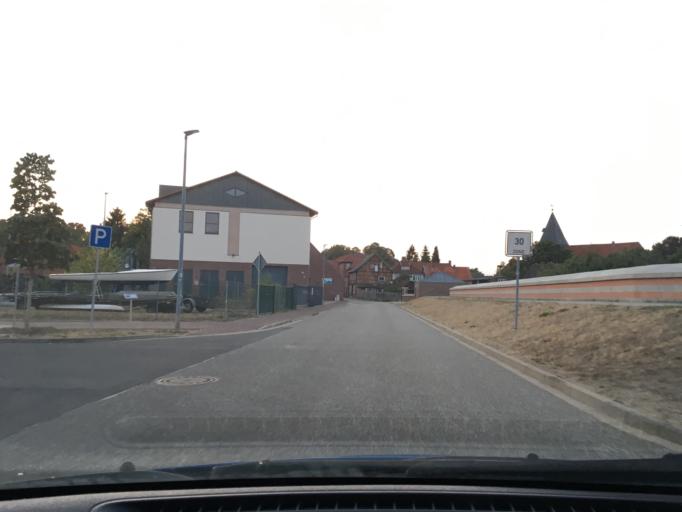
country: DE
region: Lower Saxony
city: Hitzacker
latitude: 53.1503
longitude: 11.0502
